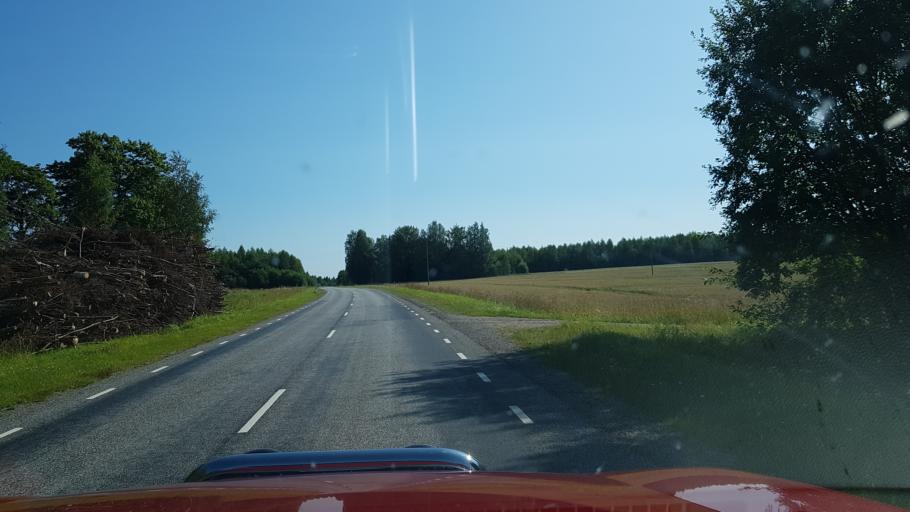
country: EE
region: Vorumaa
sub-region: Voru linn
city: Voru
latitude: 57.9754
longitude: 26.8482
